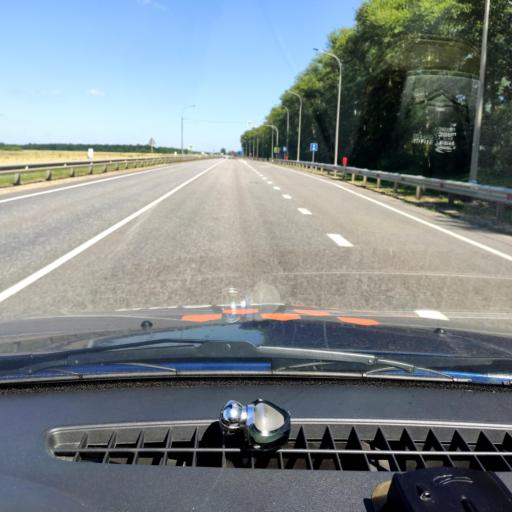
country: RU
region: Orjol
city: Pokrovskoye
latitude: 52.6201
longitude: 36.7562
